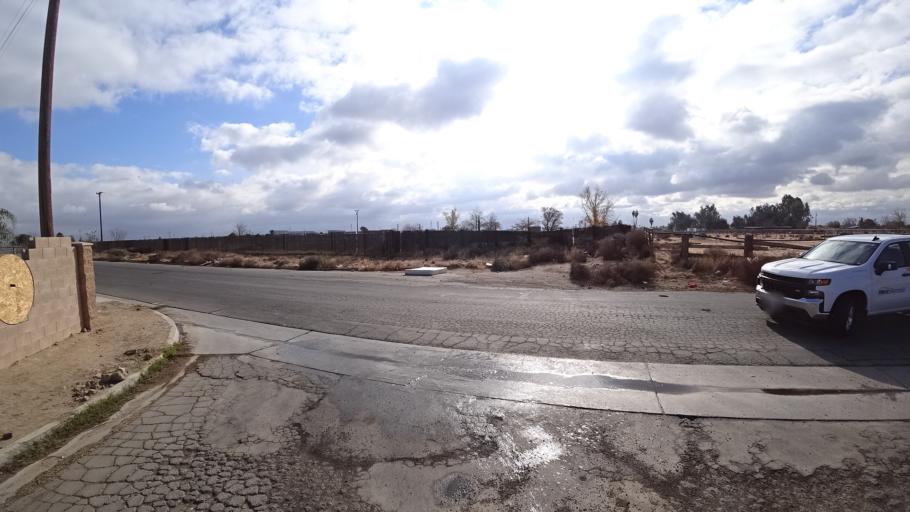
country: US
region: California
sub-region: Kern County
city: Greenfield
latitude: 35.3214
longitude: -118.9898
